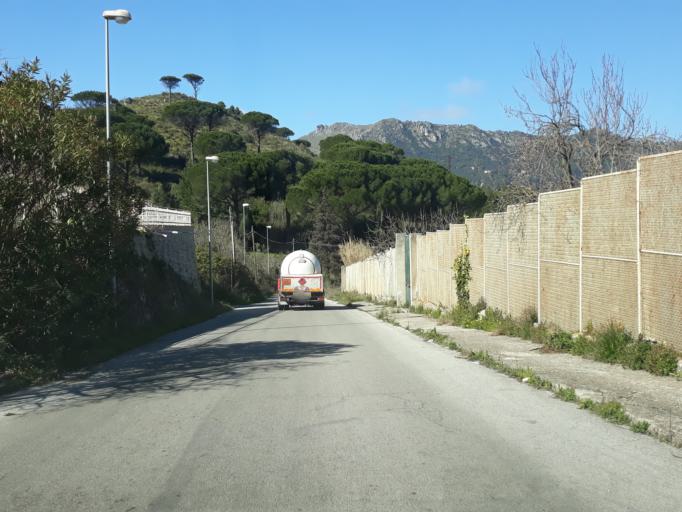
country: IT
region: Sicily
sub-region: Palermo
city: Piano dei Geli
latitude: 38.0838
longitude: 13.2695
